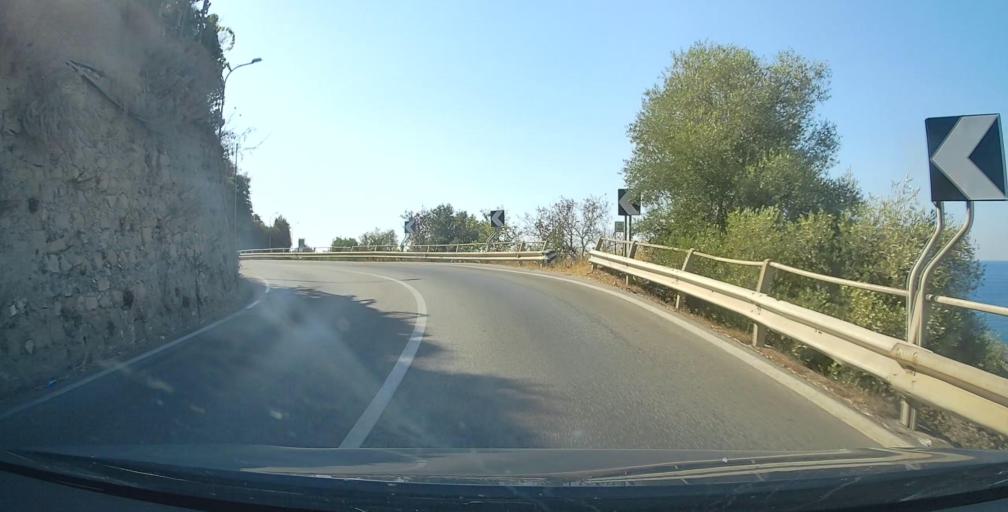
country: IT
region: Sicily
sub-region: Messina
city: Naso
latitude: 38.1532
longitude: 14.7810
